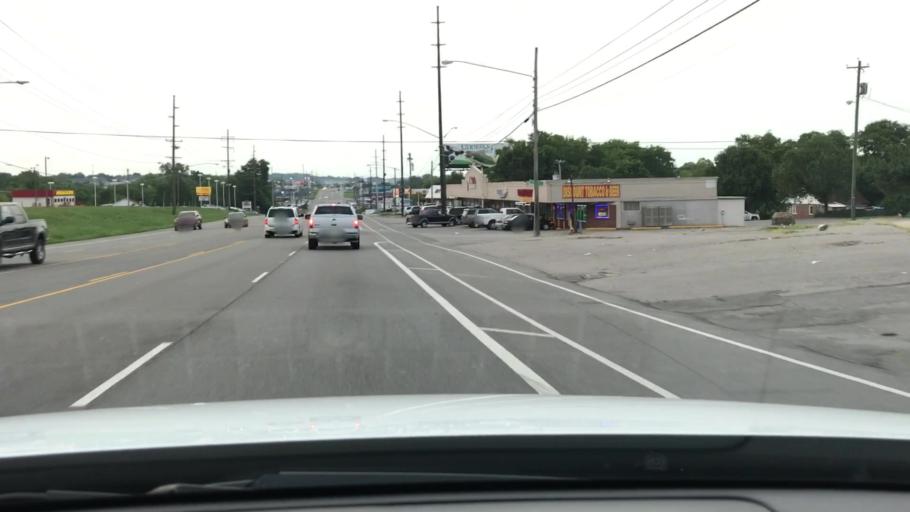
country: US
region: Tennessee
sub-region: Davidson County
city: Goodlettsville
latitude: 36.2809
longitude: -86.7080
